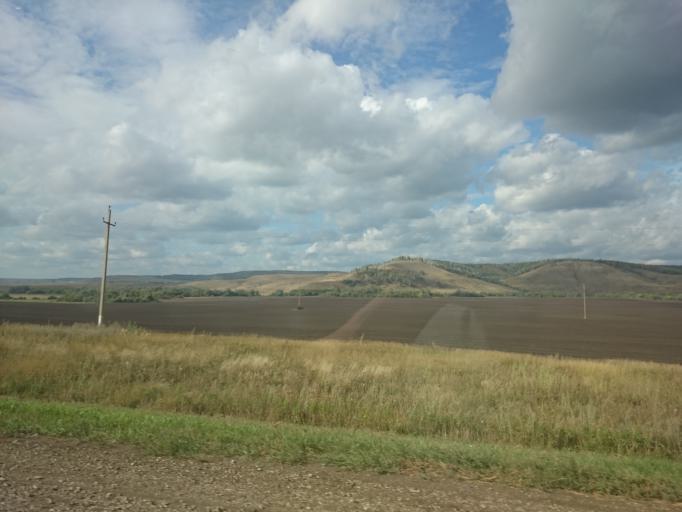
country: RU
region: Samara
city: Kamyshla
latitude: 54.0724
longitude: 52.2115
